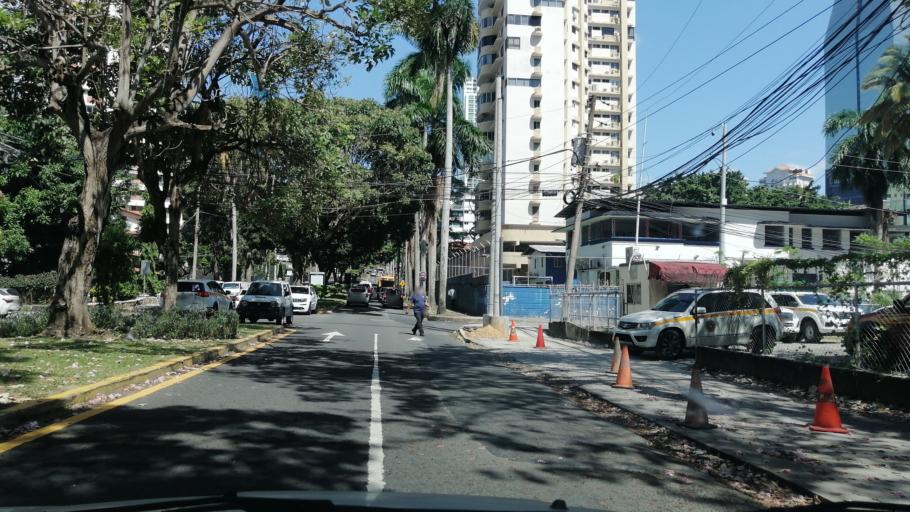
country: PA
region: Panama
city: Panama
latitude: 8.9760
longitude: -79.5265
